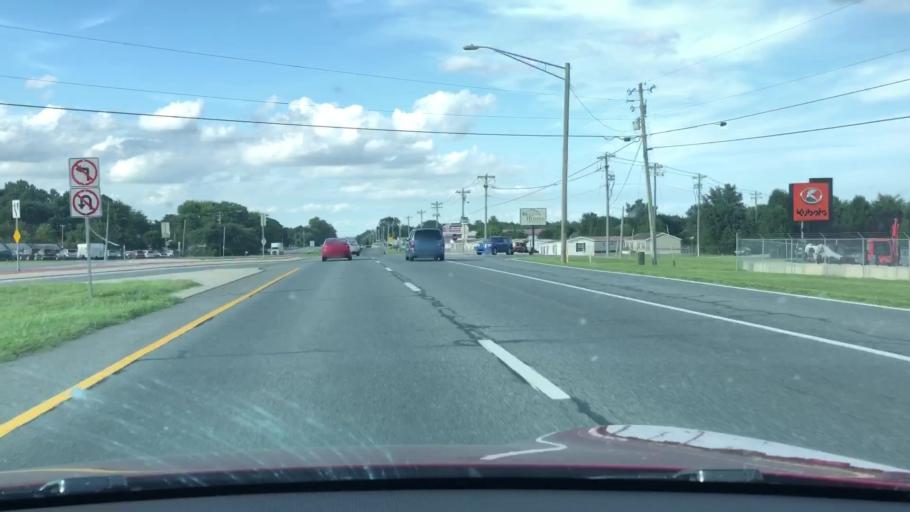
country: US
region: Delaware
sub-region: Kent County
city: Felton
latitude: 39.0234
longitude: -75.5630
